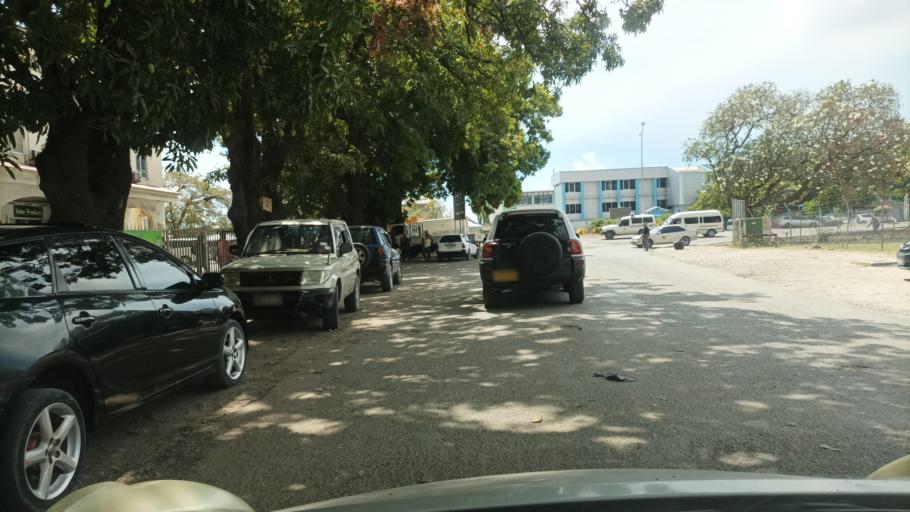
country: SB
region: Guadalcanal
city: Honiara
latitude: -9.4309
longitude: 159.9498
